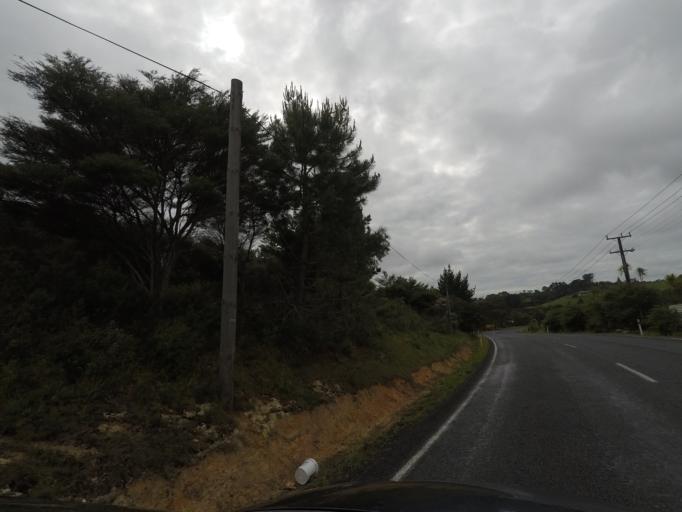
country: NZ
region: Auckland
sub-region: Auckland
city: Rosebank
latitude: -36.8327
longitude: 174.5762
